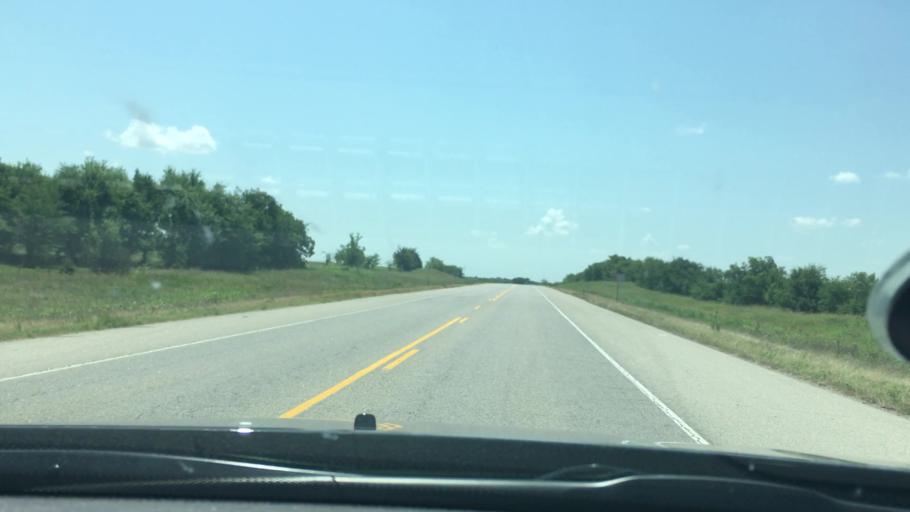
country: US
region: Oklahoma
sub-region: Pontotoc County
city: Ada
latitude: 34.7157
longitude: -96.6229
